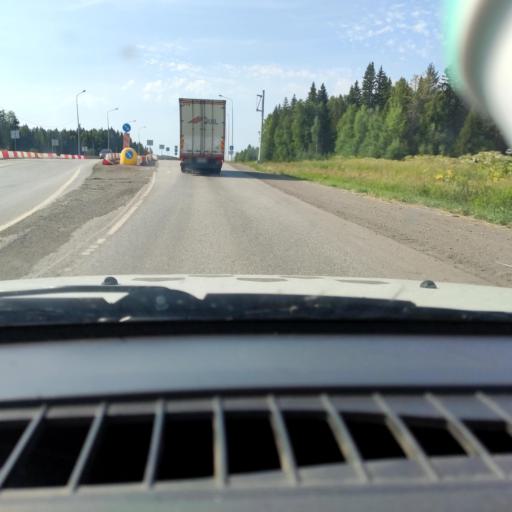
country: RU
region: Perm
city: Kukushtan
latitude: 57.6270
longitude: 56.4702
